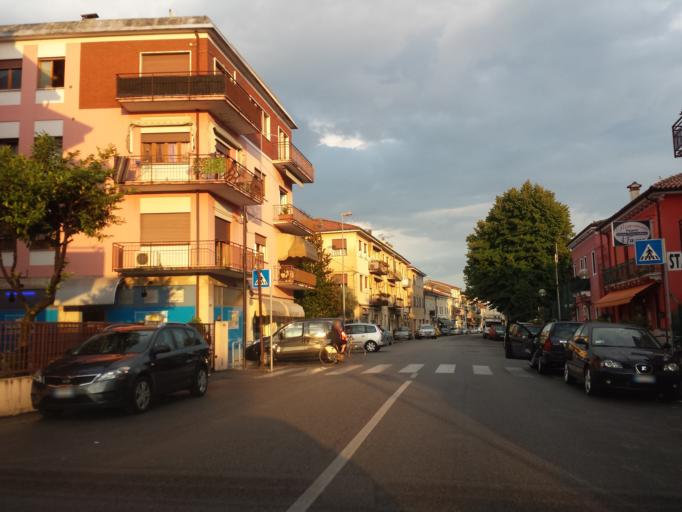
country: IT
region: Veneto
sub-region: Provincia di Vicenza
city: Villaggio Montegrappa
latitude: 45.5400
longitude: 11.5823
